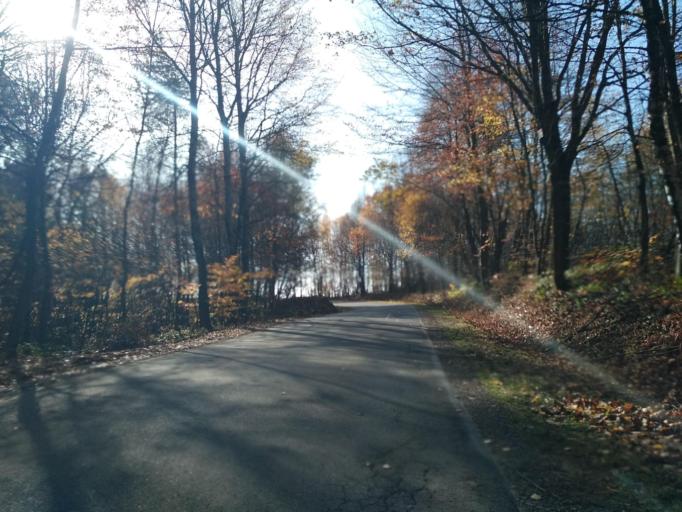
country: PL
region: Subcarpathian Voivodeship
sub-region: Powiat brzozowski
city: Wesola
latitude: 49.8367
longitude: 22.1502
